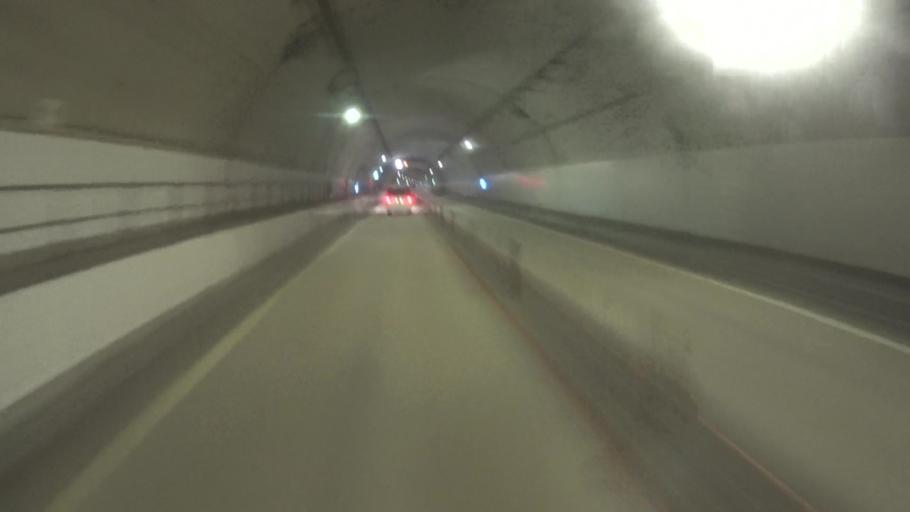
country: JP
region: Kyoto
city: Miyazu
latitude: 35.5252
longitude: 135.1781
